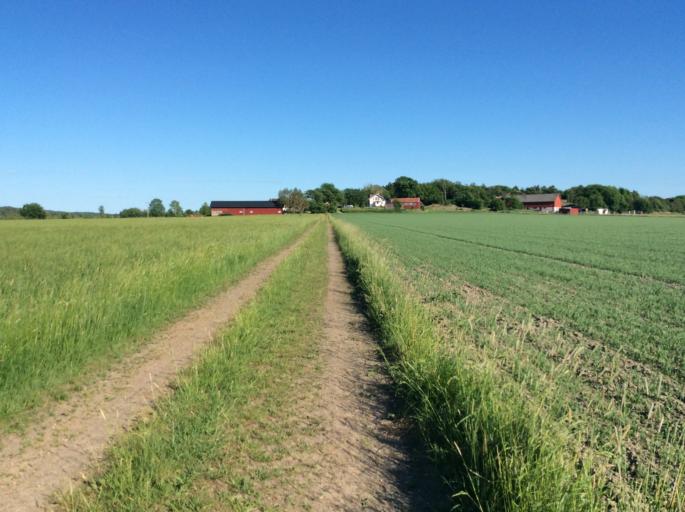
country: SE
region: Vaestra Goetaland
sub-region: Goteborg
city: Majorna
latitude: 57.7977
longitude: 11.8750
